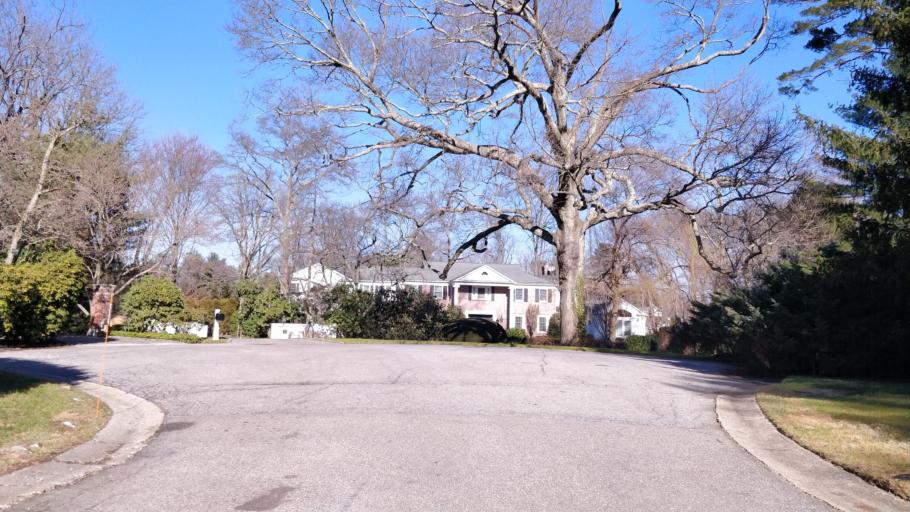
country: US
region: New York
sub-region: Nassau County
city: Glen Head
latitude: 40.8251
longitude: -73.6187
